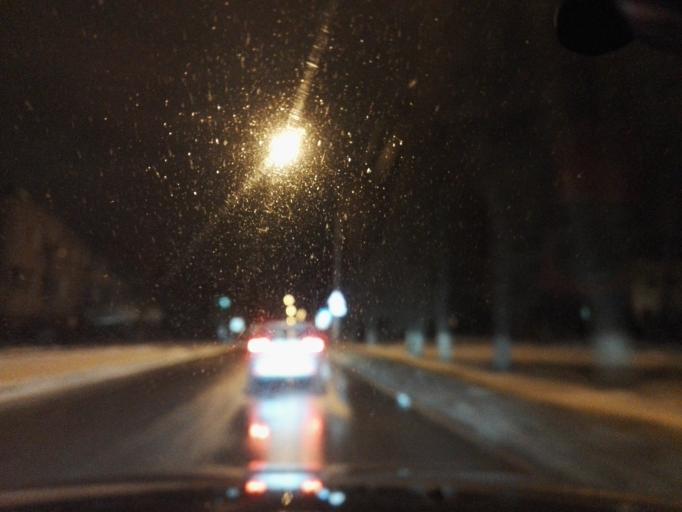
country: RU
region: Tula
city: Novomoskovsk
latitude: 54.0081
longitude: 38.2874
